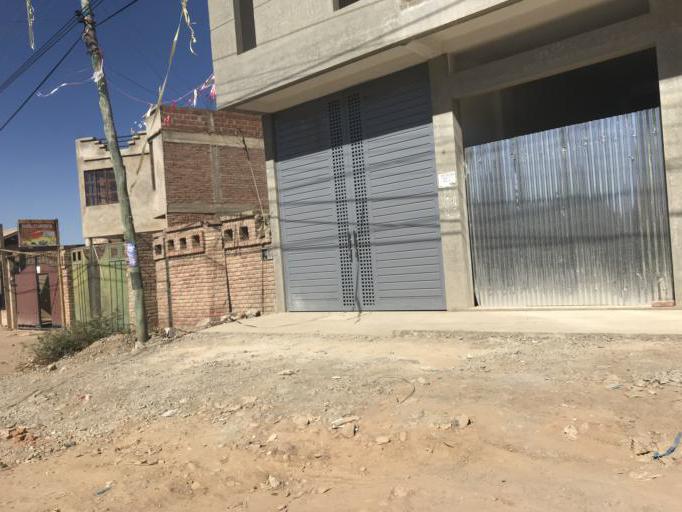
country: BO
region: Cochabamba
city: Cliza
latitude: -17.5910
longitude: -65.9299
